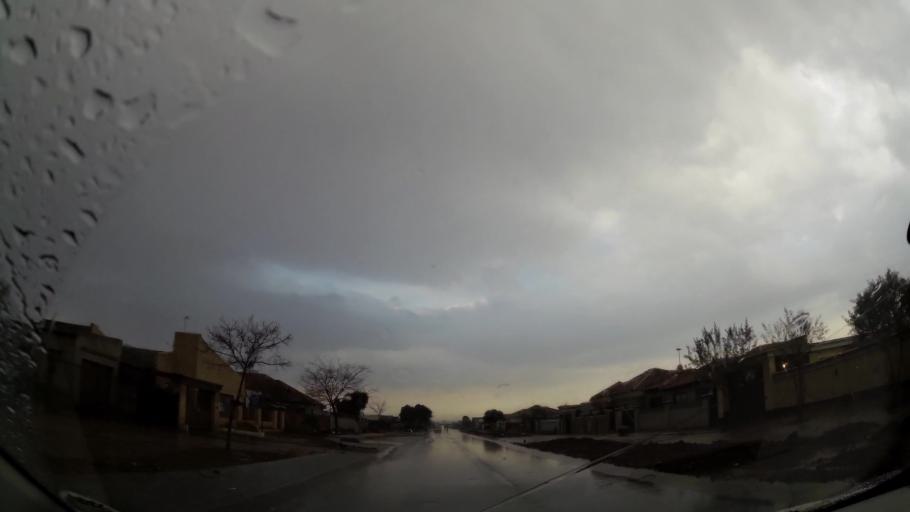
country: ZA
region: Gauteng
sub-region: Ekurhuleni Metropolitan Municipality
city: Germiston
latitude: -26.3539
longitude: 28.1410
